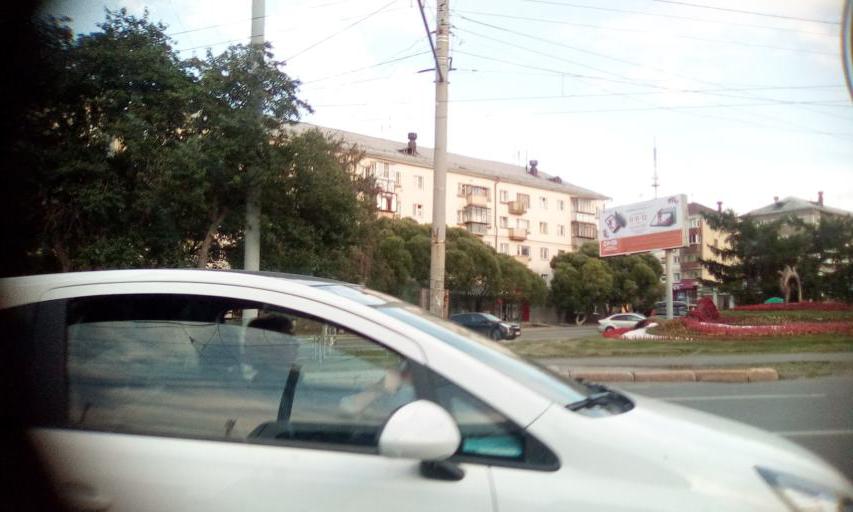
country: RU
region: Chelyabinsk
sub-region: Gorod Chelyabinsk
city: Chelyabinsk
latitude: 55.1582
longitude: 61.3981
